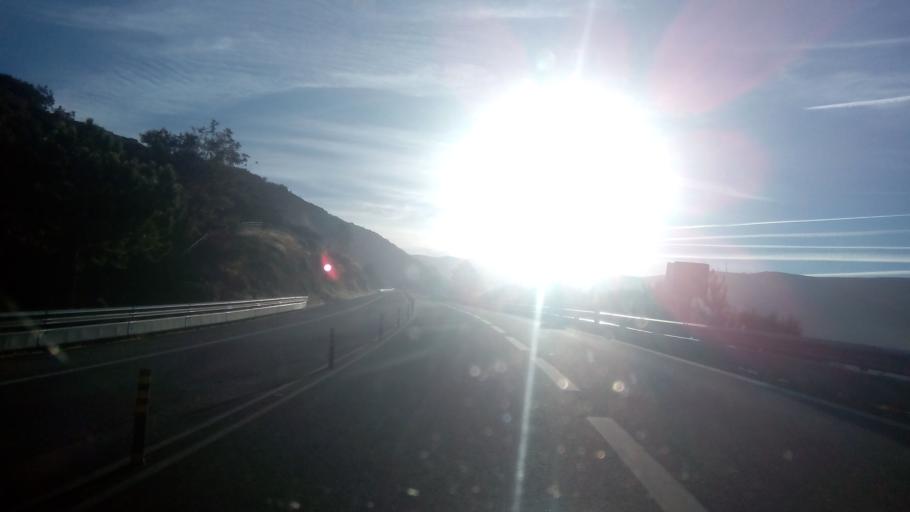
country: PT
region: Porto
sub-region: Baiao
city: Valadares
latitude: 41.2559
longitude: -7.9673
